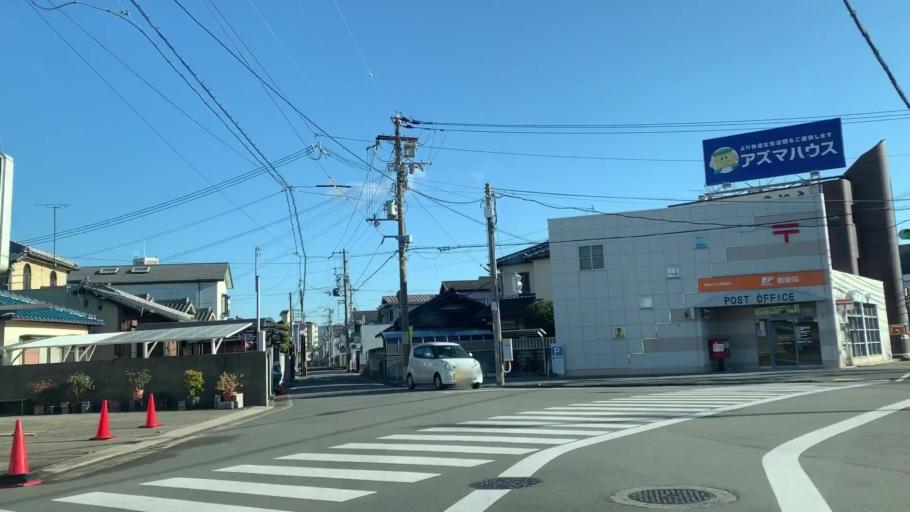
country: JP
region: Wakayama
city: Wakayama-shi
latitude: 34.2396
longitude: 135.1813
